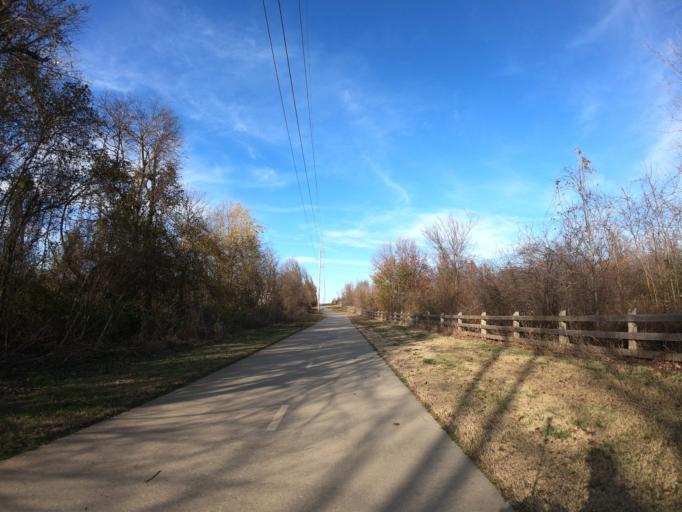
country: US
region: Arkansas
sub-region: Benton County
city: Lowell
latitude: 36.2877
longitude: -94.1654
